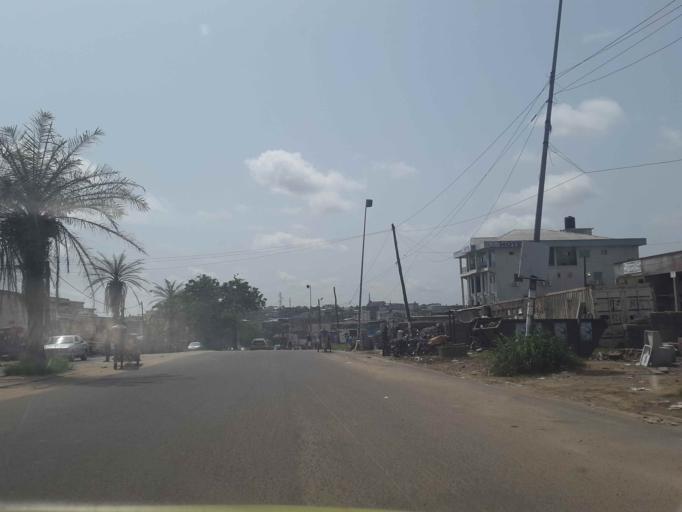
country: CM
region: Littoral
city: Douala
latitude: 4.0843
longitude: 9.7414
